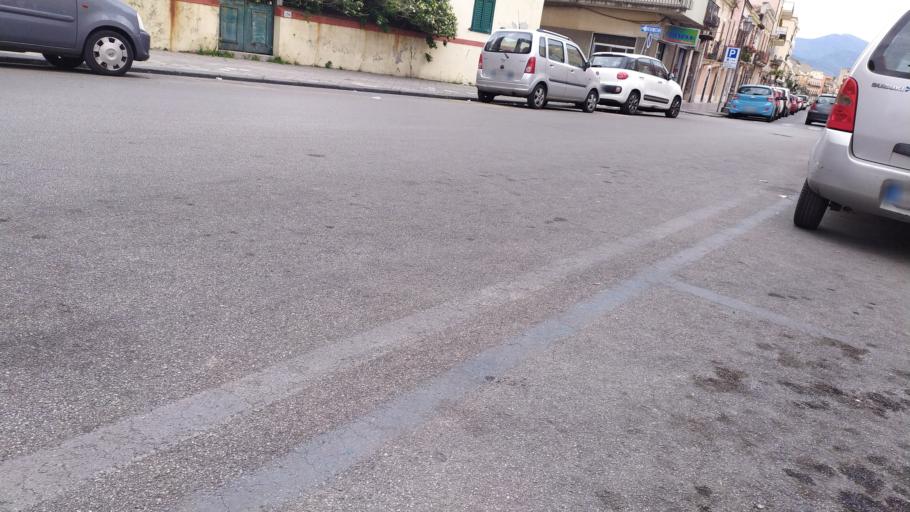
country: IT
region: Sicily
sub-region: Messina
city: Milazzo
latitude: 38.2248
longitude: 15.2406
